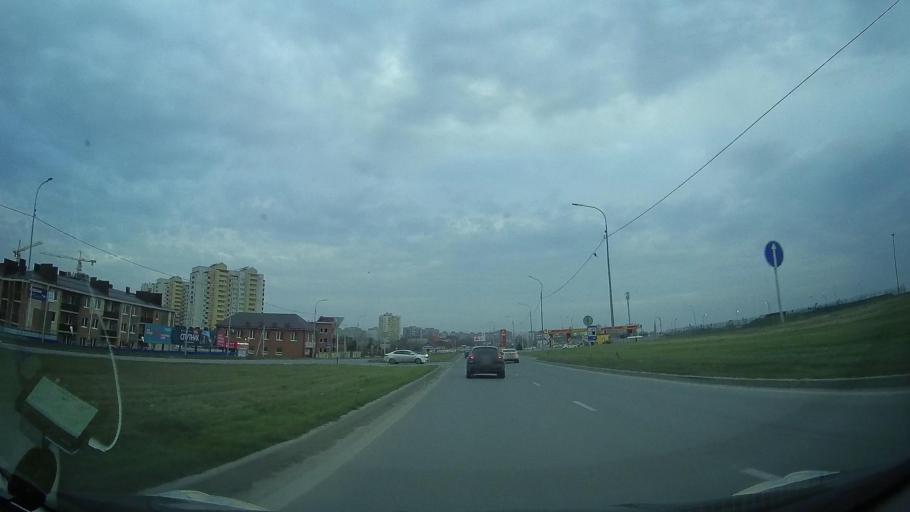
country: RU
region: Rostov
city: Severnyy
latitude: 47.3066
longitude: 39.7244
